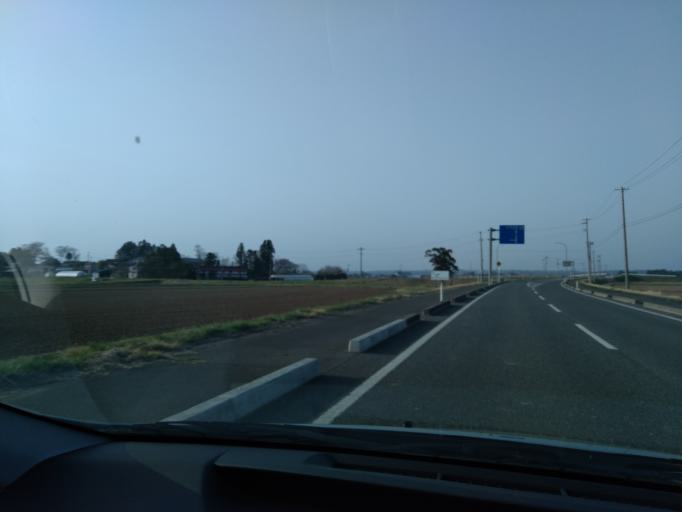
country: JP
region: Iwate
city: Ichinoseki
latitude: 38.7447
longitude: 141.1313
